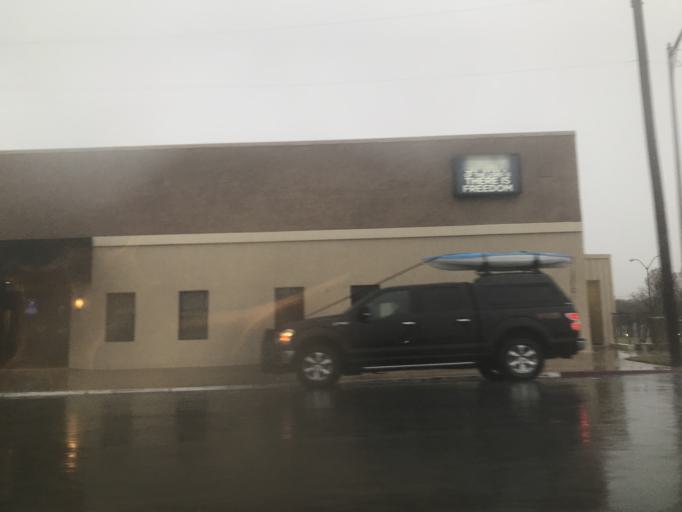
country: US
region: Texas
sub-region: Tom Green County
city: San Angelo
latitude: 31.4591
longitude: -100.4354
